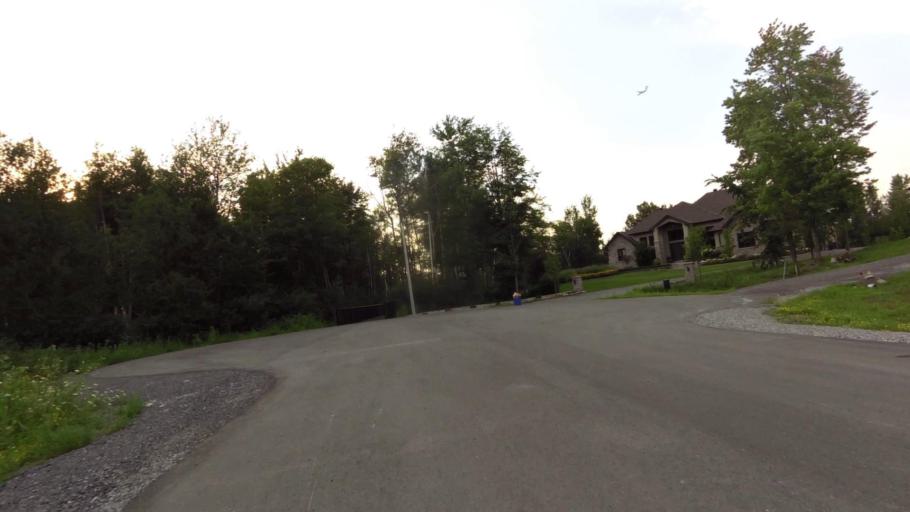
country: CA
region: Ontario
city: Ottawa
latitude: 45.2681
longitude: -75.5853
